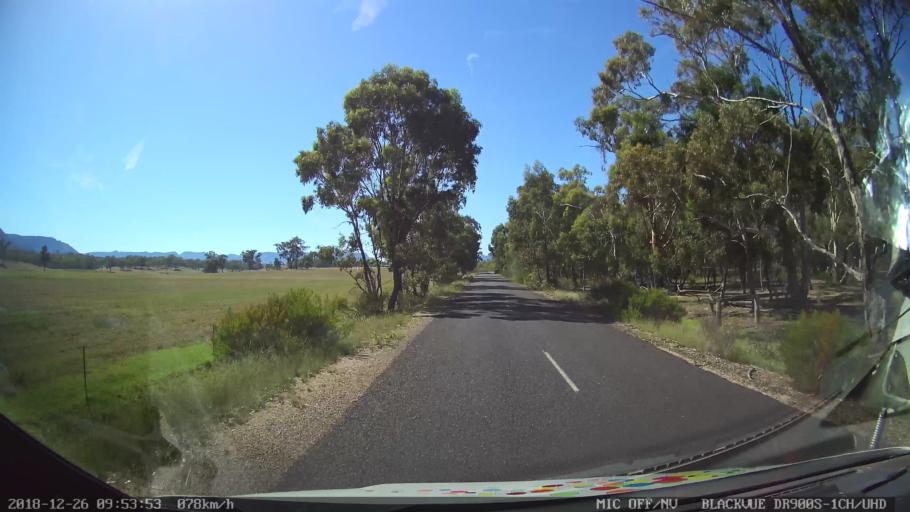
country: AU
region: New South Wales
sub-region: Mid-Western Regional
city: Kandos
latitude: -33.0251
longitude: 150.1566
